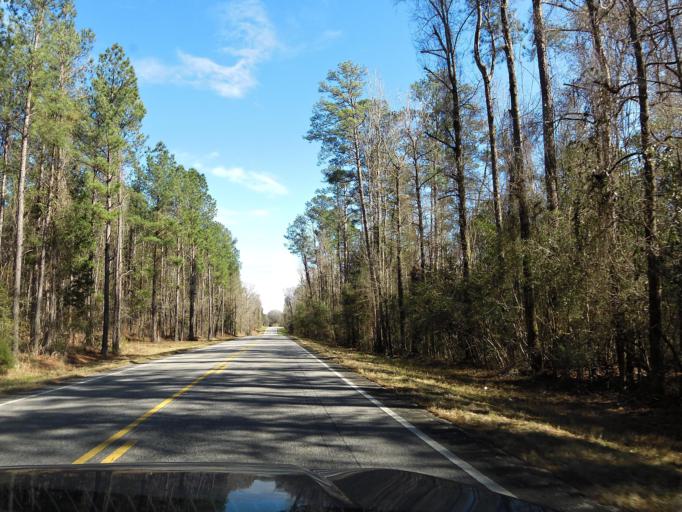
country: US
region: Alabama
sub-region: Barbour County
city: Clayton
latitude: 32.0345
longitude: -85.3884
